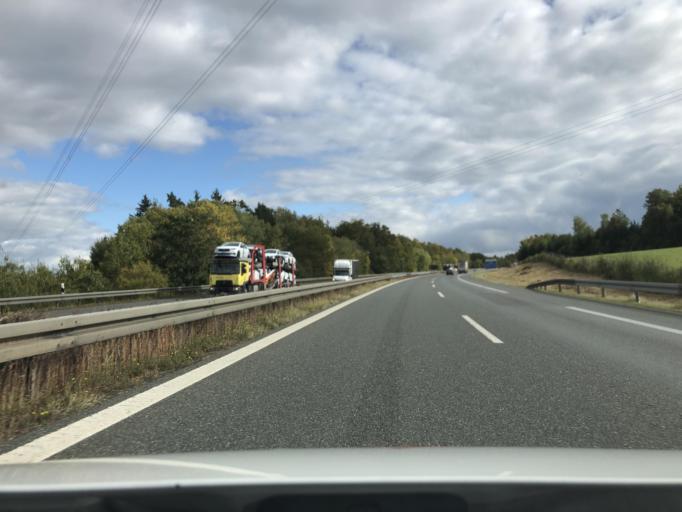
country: DE
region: Bavaria
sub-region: Upper Palatinate
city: Ursensollen
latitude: 49.4072
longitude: 11.7766
